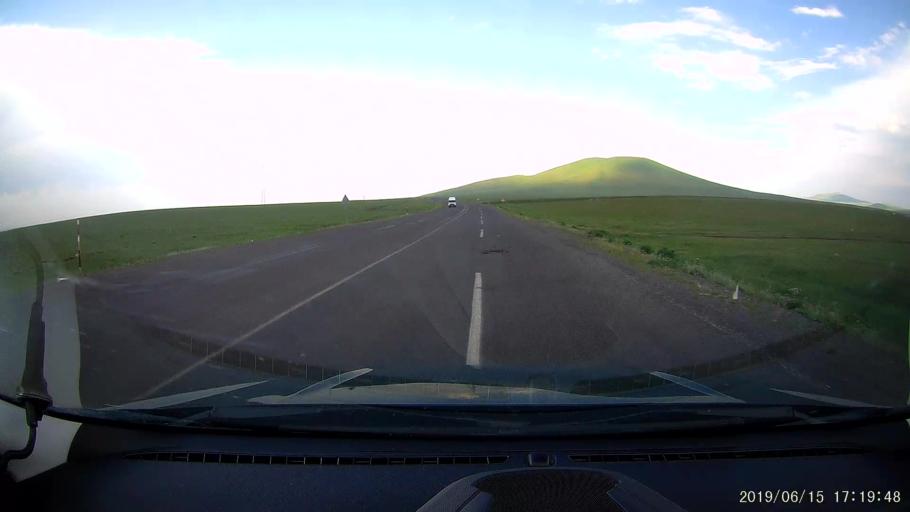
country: TR
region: Kars
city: Kars
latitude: 40.6162
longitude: 43.2866
